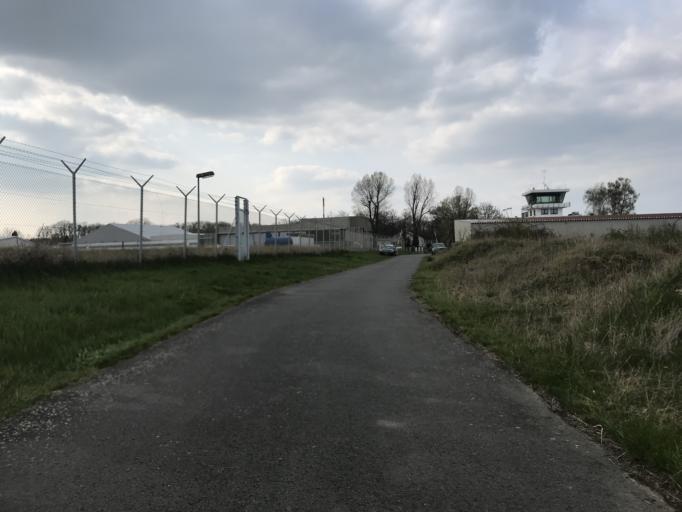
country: DE
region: Rheinland-Pfalz
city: Wackernheim
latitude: 49.9713
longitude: 8.1529
